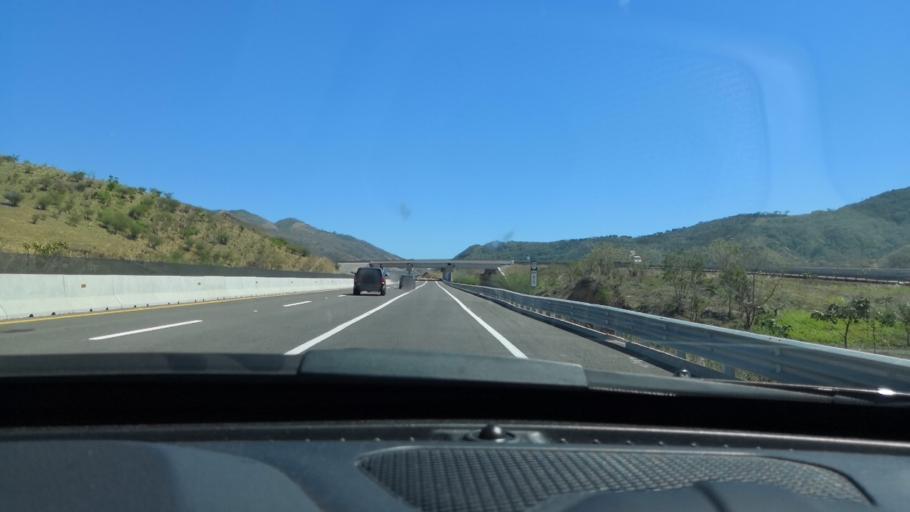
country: MX
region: Nayarit
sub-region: Compostela
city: Juan Escutia (Borbollon)
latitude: 21.1398
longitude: -104.9238
